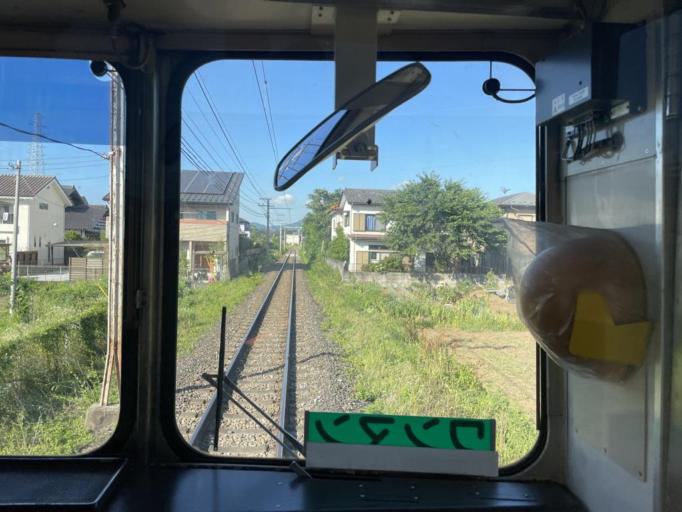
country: JP
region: Saitama
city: Chichibu
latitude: 35.9774
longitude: 139.0748
